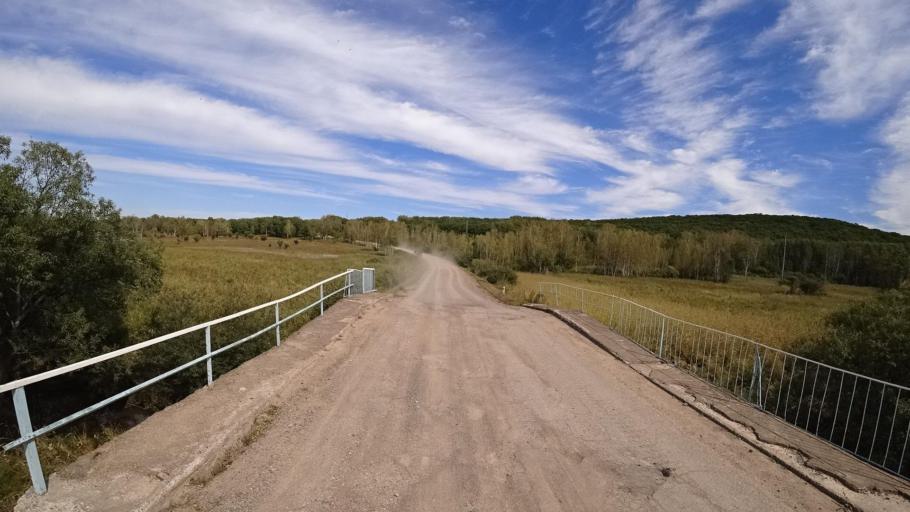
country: RU
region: Primorskiy
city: Yakovlevka
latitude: 44.6787
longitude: 133.6151
